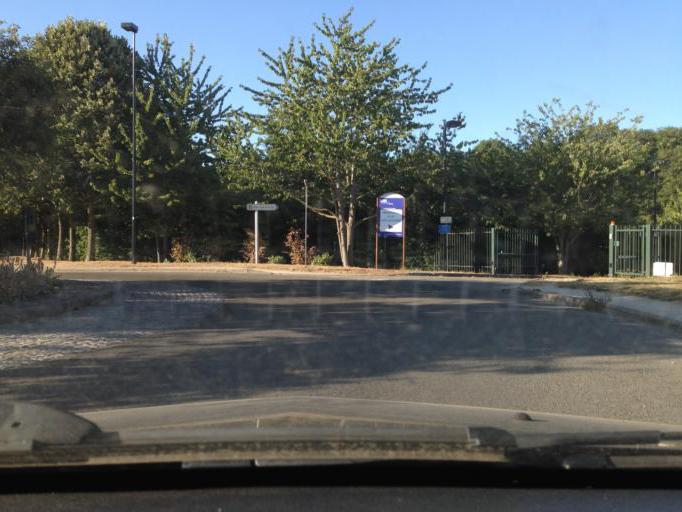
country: FR
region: Ile-de-France
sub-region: Departement des Yvelines
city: Chateaufort
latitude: 48.7285
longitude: 2.0815
